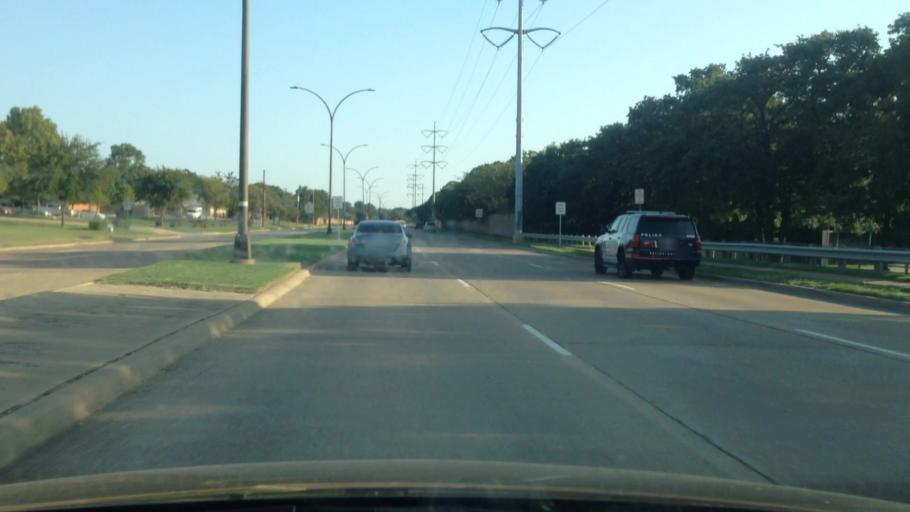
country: US
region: Texas
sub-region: Tarrant County
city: Dalworthington Gardens
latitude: 32.6967
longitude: -97.1904
